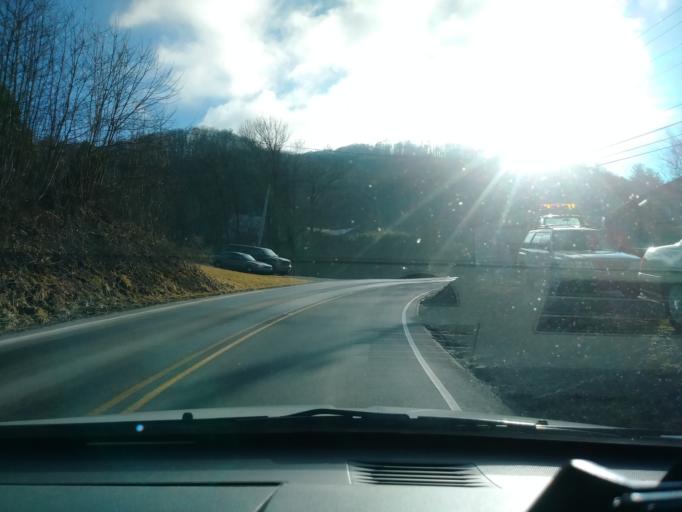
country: US
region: North Carolina
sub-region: Avery County
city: Banner Elk
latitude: 36.1725
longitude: -81.9121
